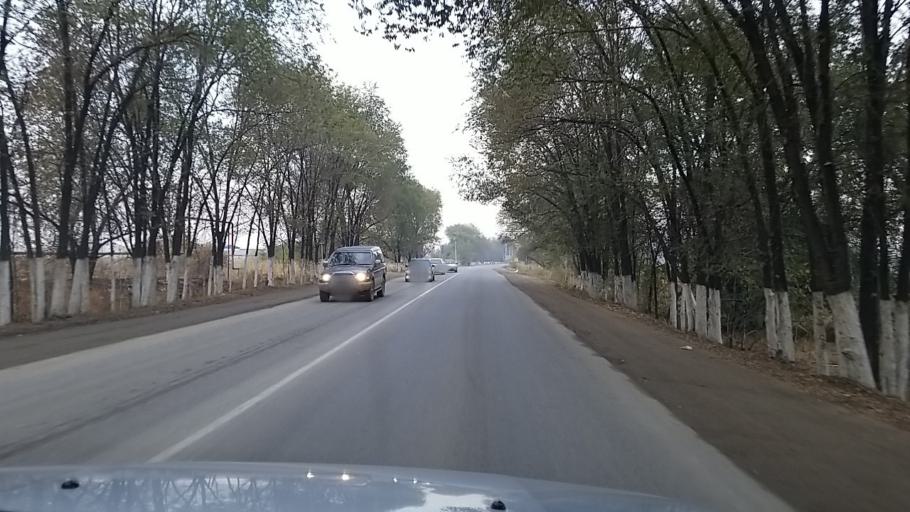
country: KZ
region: Almaty Oblysy
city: Burunday
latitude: 43.3560
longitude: 76.7974
